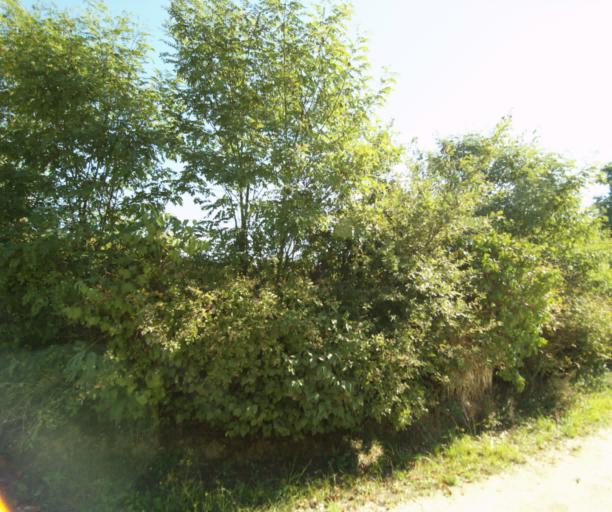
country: FR
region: Midi-Pyrenees
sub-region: Departement du Gers
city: Cazaubon
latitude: 43.9388
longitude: -0.0337
